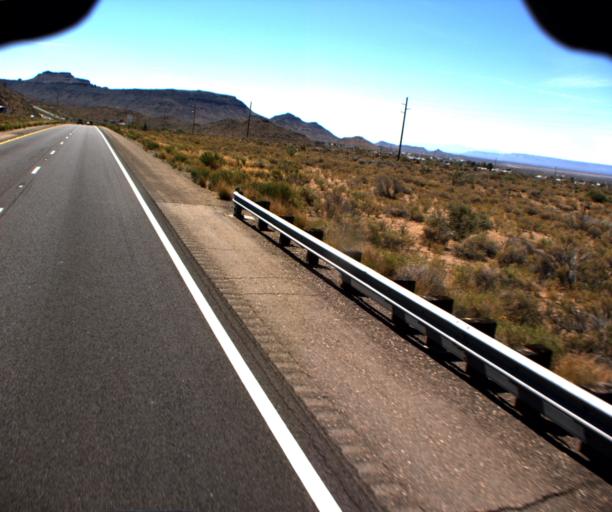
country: US
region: Arizona
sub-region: Mohave County
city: Golden Valley
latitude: 35.2482
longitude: -114.1519
